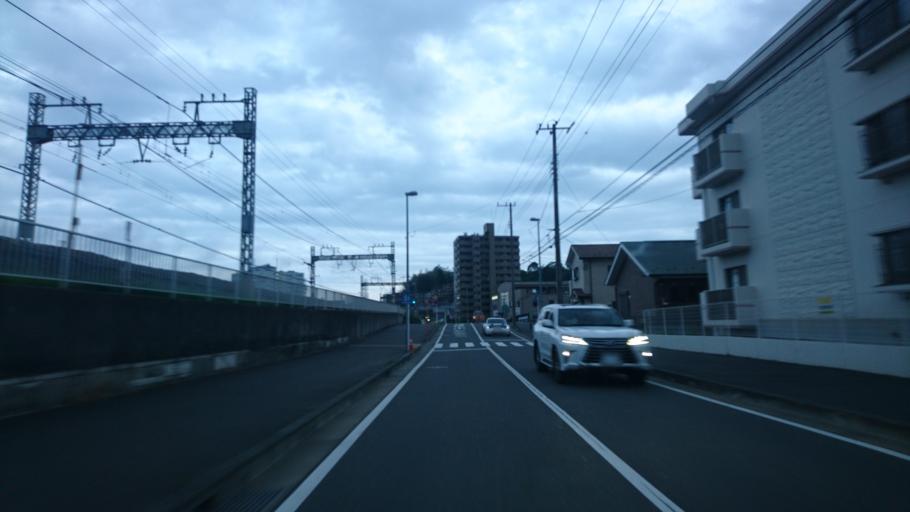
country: JP
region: Kanagawa
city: Fujisawa
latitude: 35.3531
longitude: 139.4740
